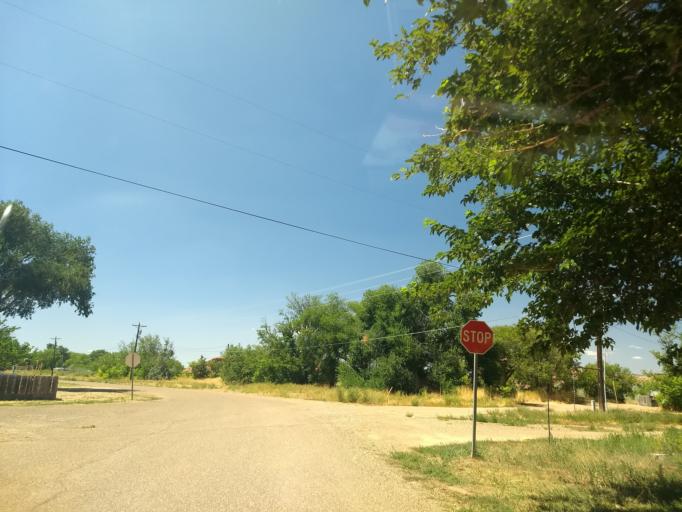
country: US
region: Arizona
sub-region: Coconino County
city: Fredonia
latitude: 36.9543
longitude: -112.5283
